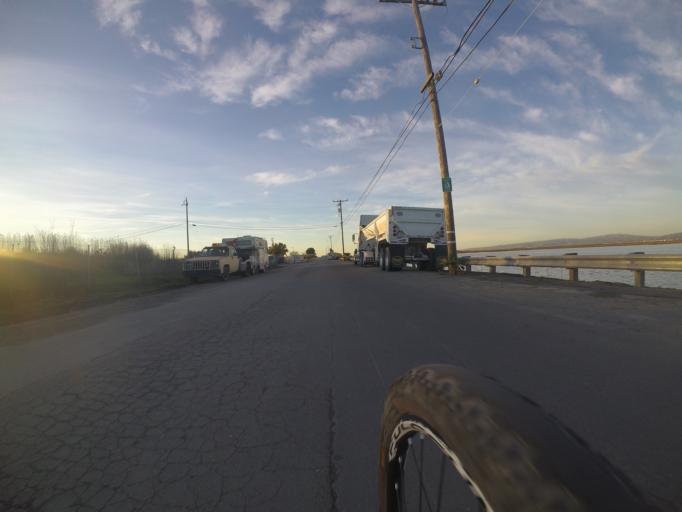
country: US
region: California
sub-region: Santa Clara County
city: Milpitas
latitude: 37.4332
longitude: -121.9671
